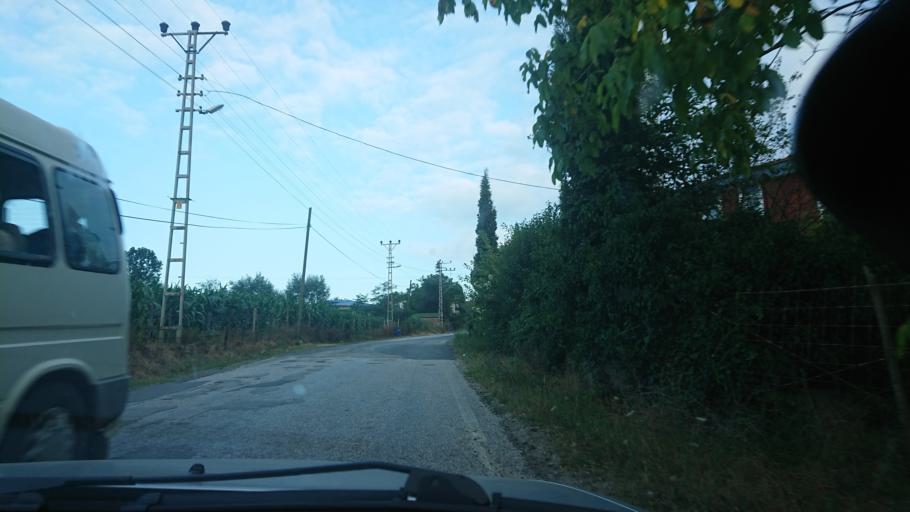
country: TR
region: Samsun
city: Tekkekoy
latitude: 41.1725
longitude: 36.5305
